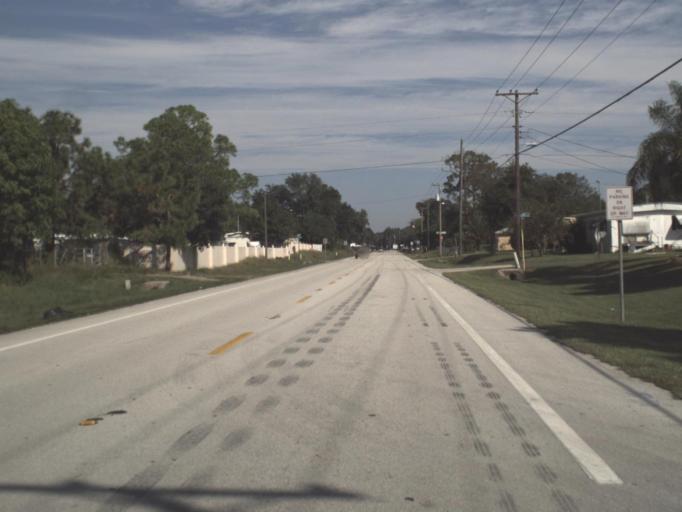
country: US
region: Florida
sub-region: Highlands County
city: Sebring
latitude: 27.5530
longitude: -81.4532
